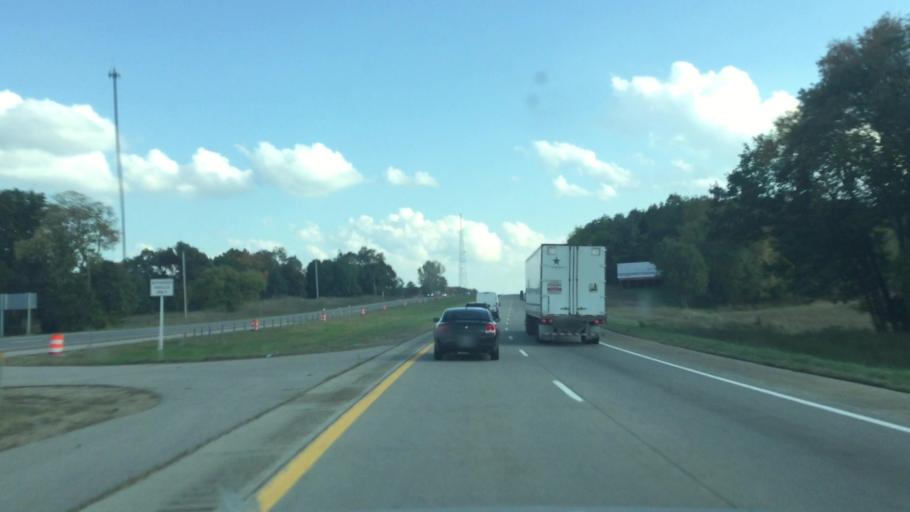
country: US
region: Michigan
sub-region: Calhoun County
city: Albion
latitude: 42.2802
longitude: -84.7895
